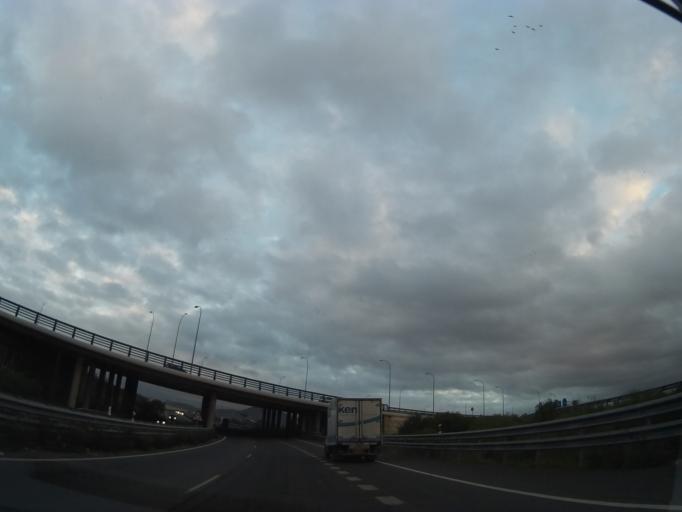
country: ES
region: Andalusia
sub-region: Provincia de Malaga
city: Alhaurin de la Torre
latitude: 36.7077
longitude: -4.5123
